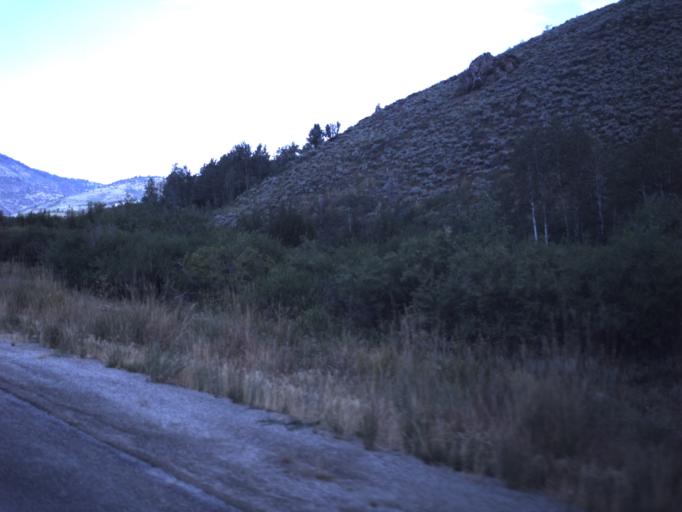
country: US
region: Utah
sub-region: Cache County
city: Richmond
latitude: 41.8892
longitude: -111.5652
